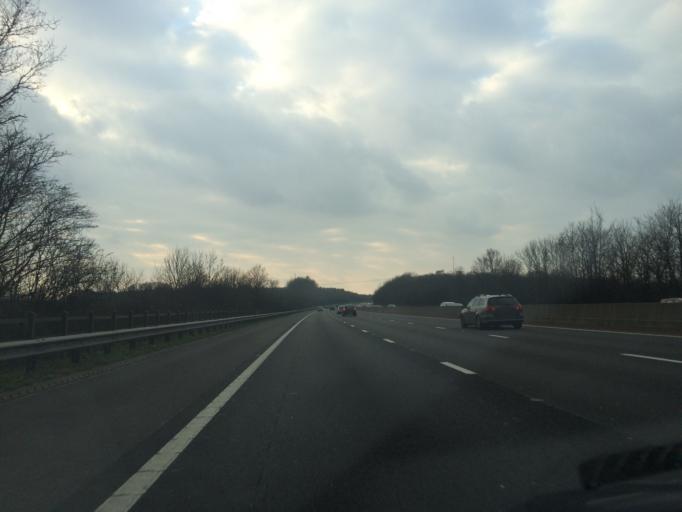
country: GB
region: England
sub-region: West Berkshire
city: Lambourn
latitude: 51.4730
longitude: -1.5350
